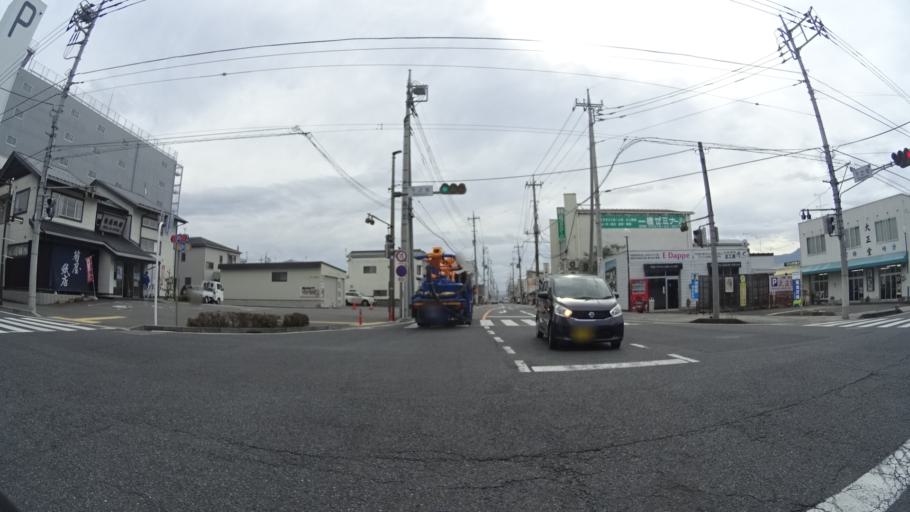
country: JP
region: Gunma
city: Numata
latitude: 36.6435
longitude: 139.0426
